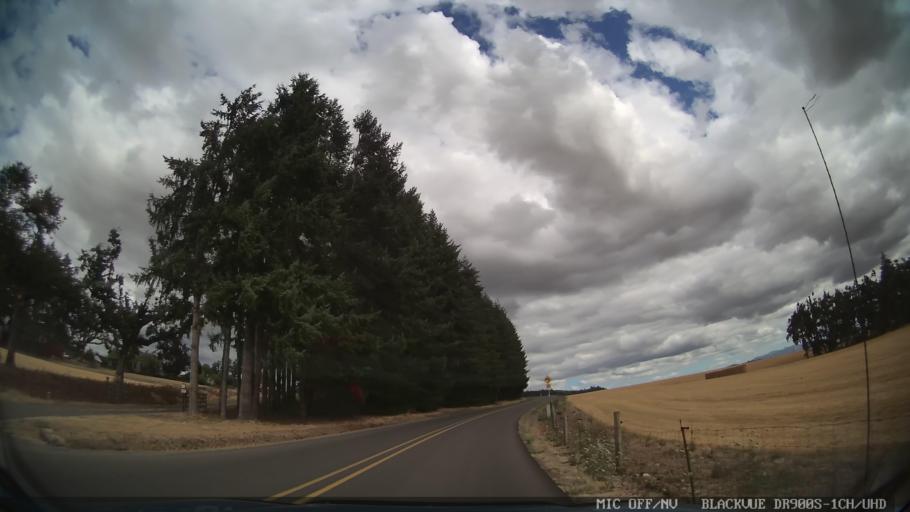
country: US
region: Oregon
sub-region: Marion County
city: Sublimity
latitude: 44.8677
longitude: -122.7469
